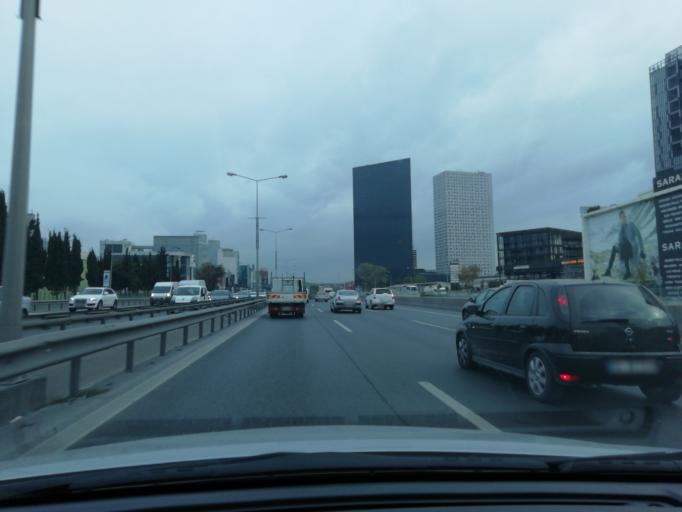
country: TR
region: Istanbul
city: Mahmutbey
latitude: 41.0508
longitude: 28.8087
